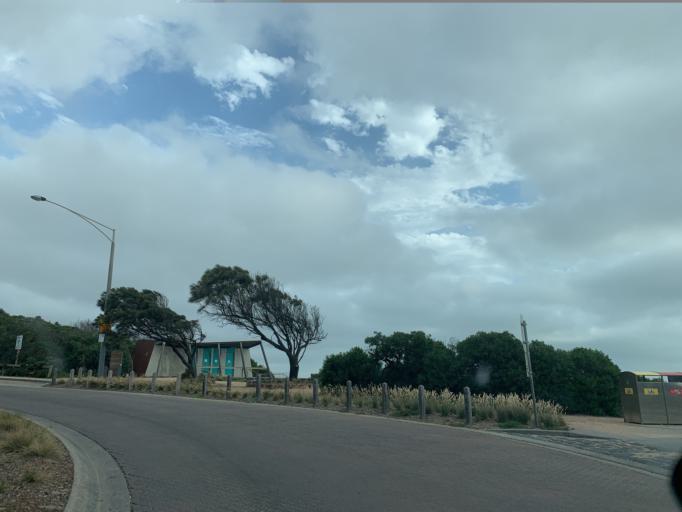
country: AU
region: Victoria
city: Hampton
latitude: -37.9466
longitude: 144.9973
